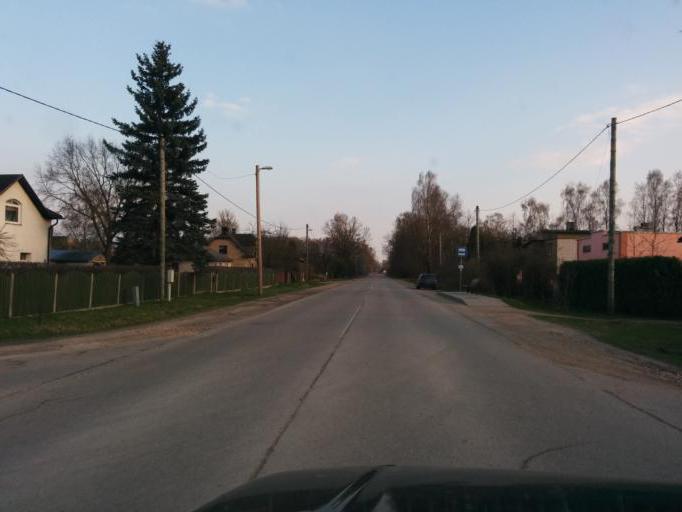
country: LV
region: Jelgava
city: Jelgava
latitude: 56.6648
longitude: 23.7347
